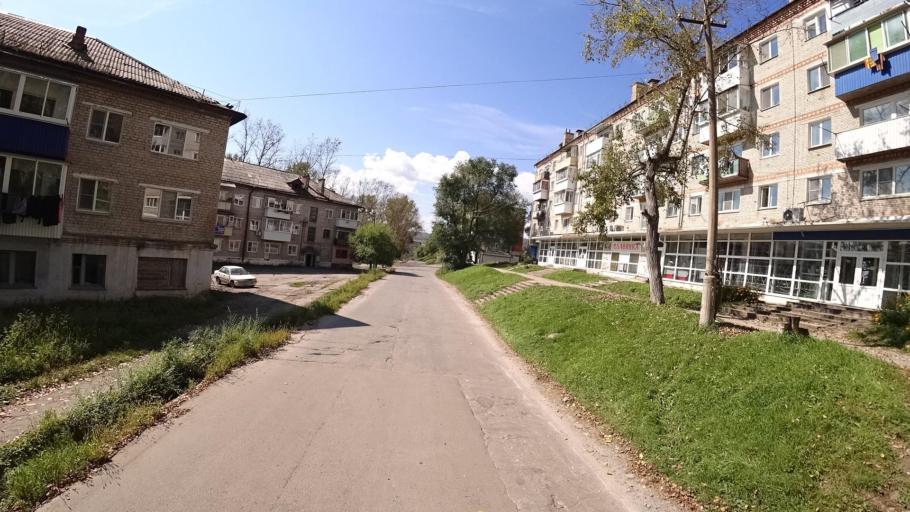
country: RU
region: Jewish Autonomous Oblast
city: Londoko
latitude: 49.0132
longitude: 131.8857
